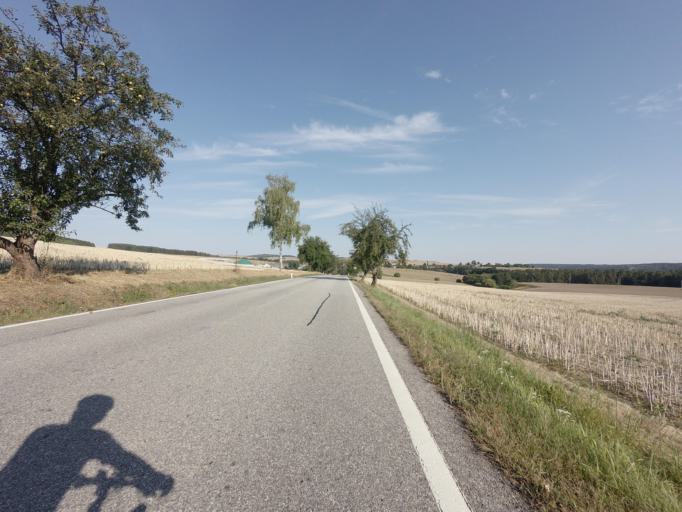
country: CZ
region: Jihocesky
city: Tyn nad Vltavou
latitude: 49.2713
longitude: 14.4060
